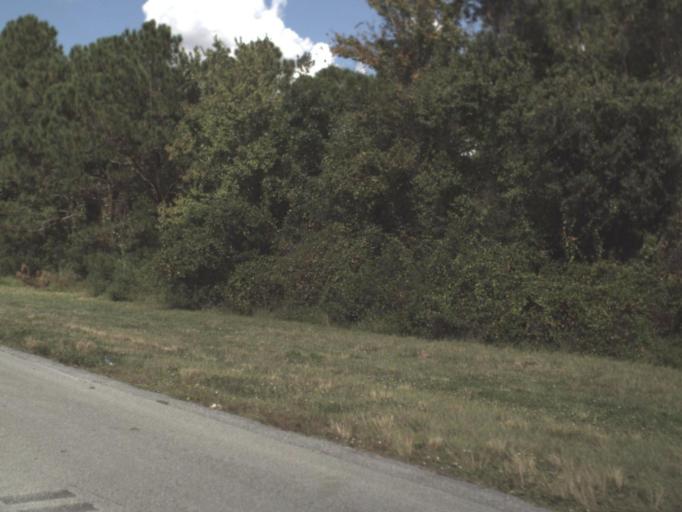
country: US
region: Florida
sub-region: Indian River County
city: Fellsmere
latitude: 27.6533
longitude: -80.8609
